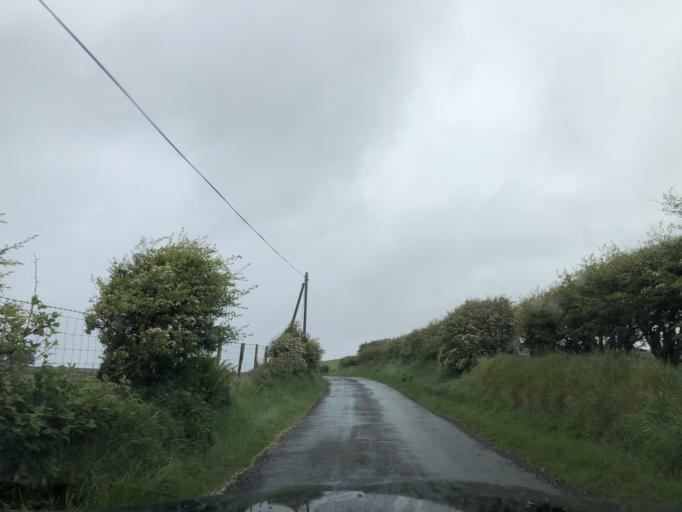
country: GB
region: Northern Ireland
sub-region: Moyle District
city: Ballycastle
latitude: 55.2027
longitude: -6.1723
